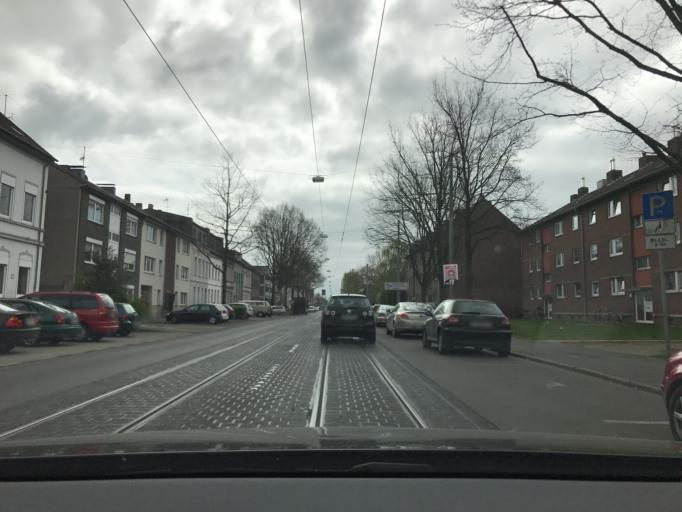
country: DE
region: North Rhine-Westphalia
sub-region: Regierungsbezirk Dusseldorf
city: Krefeld
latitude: 51.3126
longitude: 6.5801
